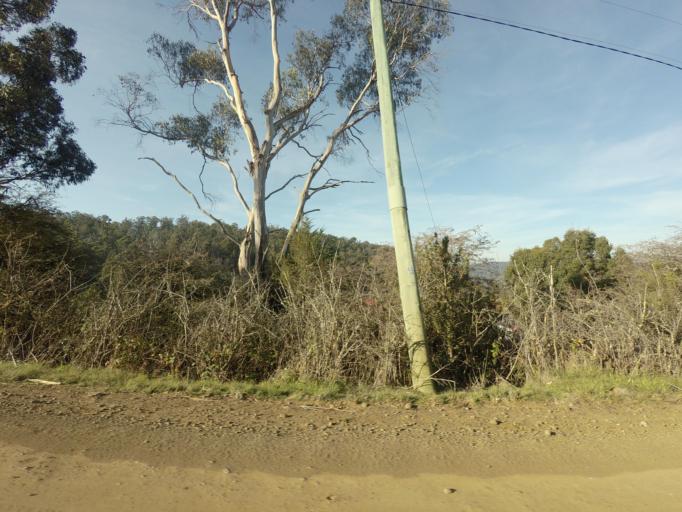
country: AU
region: Tasmania
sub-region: Brighton
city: Bridgewater
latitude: -42.4732
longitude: 147.3824
